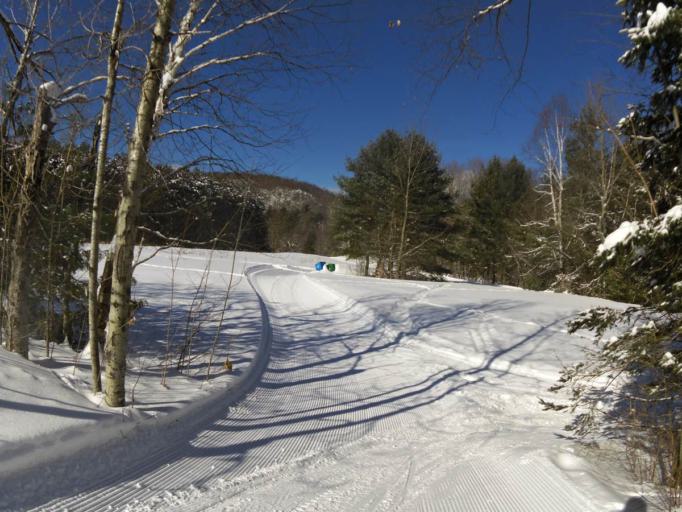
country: CA
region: Quebec
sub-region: Outaouais
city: Wakefield
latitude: 45.6029
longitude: -76.0206
